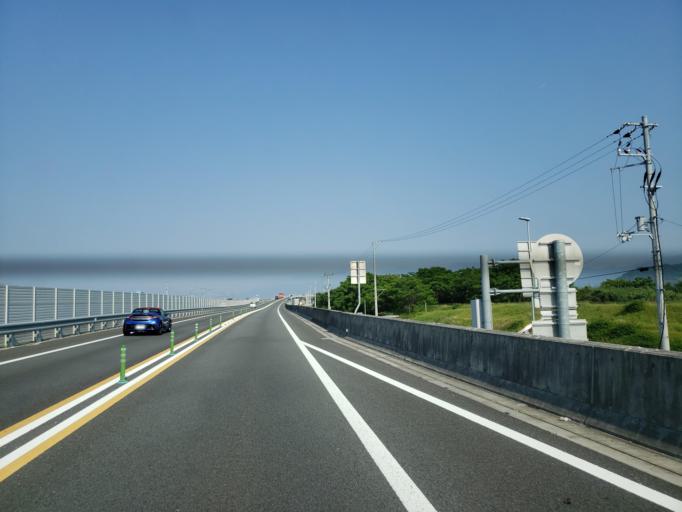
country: JP
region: Ehime
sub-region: Shikoku-chuo Shi
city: Matsuyama
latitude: 33.8064
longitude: 132.7536
